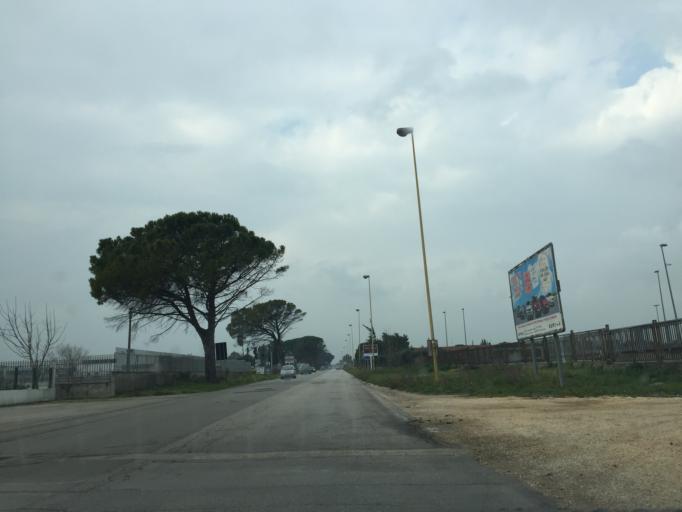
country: IT
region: Apulia
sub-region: Provincia di Foggia
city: Foggia
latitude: 41.4480
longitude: 15.5104
